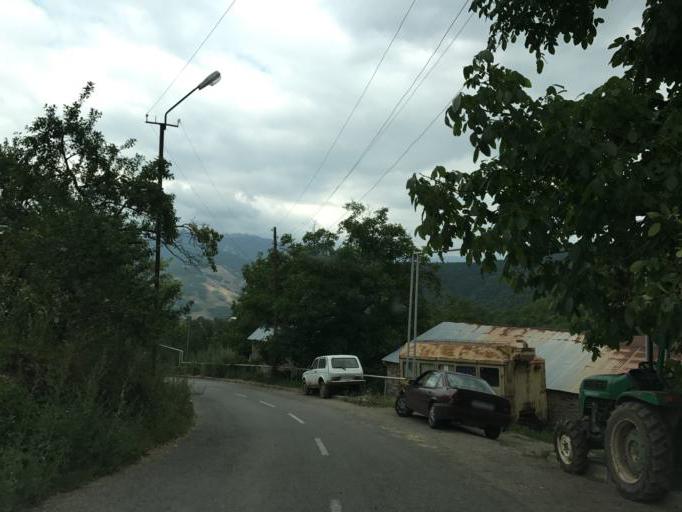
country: AM
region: Tavush
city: Haghartsin
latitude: 40.7293
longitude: 44.9977
